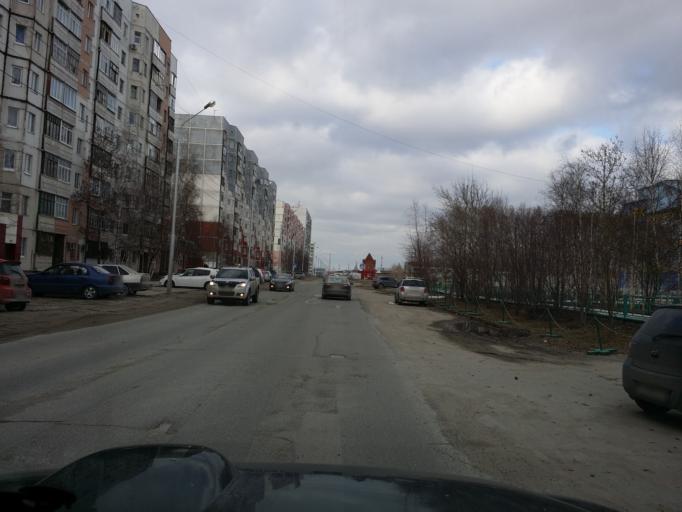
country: RU
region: Khanty-Mansiyskiy Avtonomnyy Okrug
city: Nizhnevartovsk
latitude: 60.9439
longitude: 76.6111
